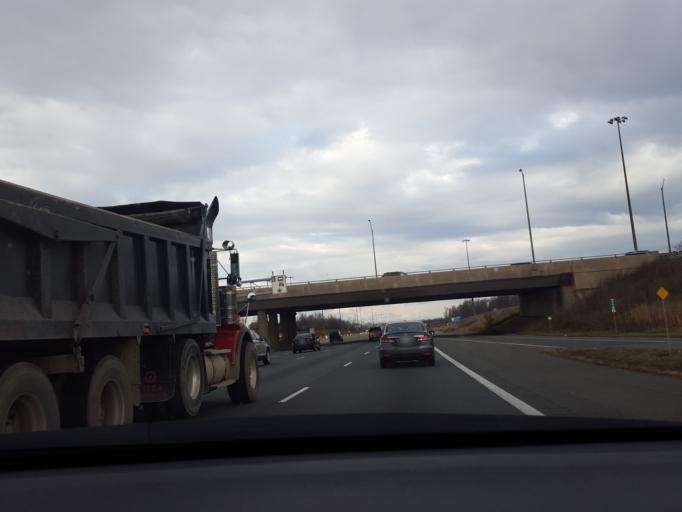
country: CA
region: Ontario
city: Mississauga
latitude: 43.5999
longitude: -79.6450
